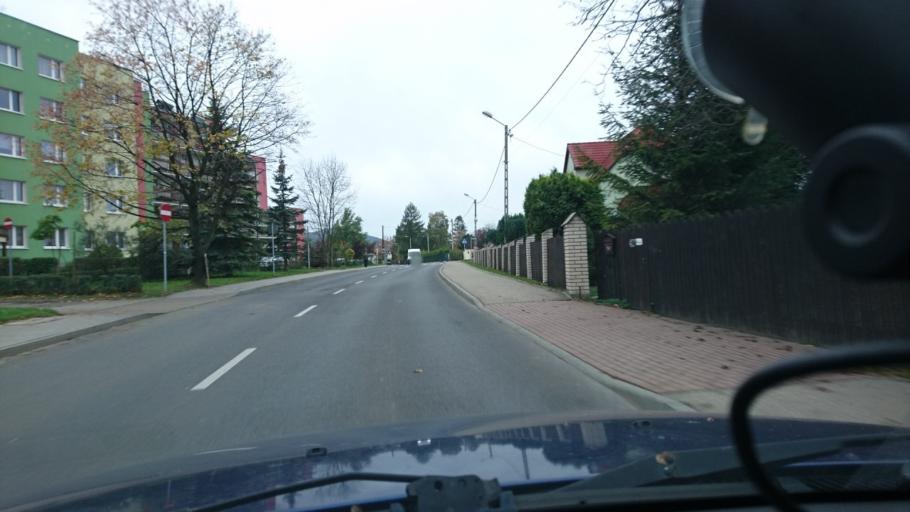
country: PL
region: Silesian Voivodeship
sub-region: Bielsko-Biala
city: Bielsko-Biala
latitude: 49.8025
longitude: 19.0260
